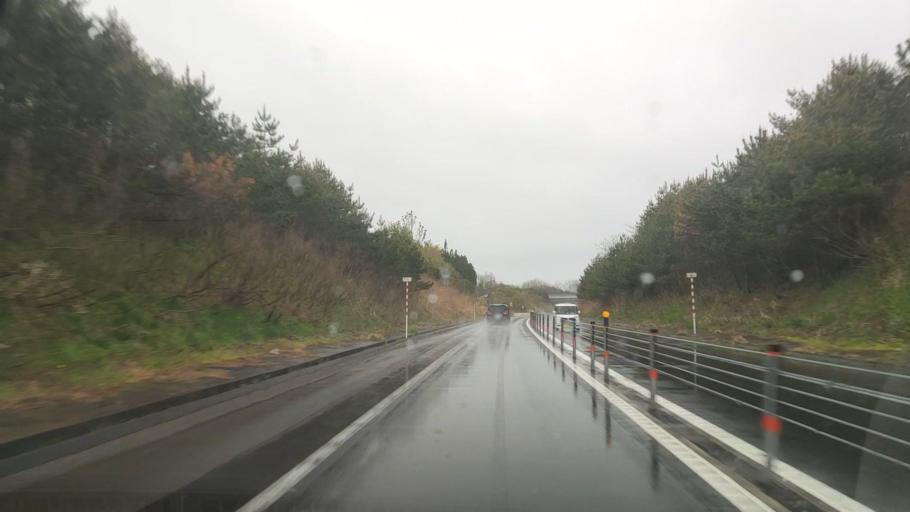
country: JP
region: Akita
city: Noshiromachi
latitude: 40.1631
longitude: 140.0436
